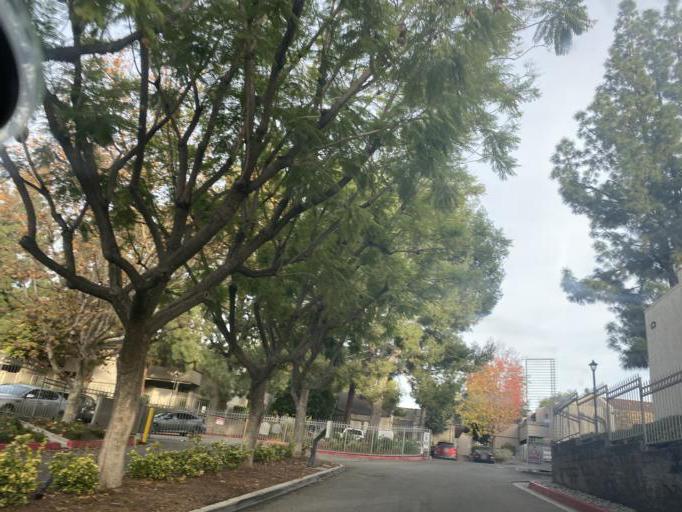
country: US
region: California
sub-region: Orange County
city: Brea
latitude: 33.9041
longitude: -117.8832
